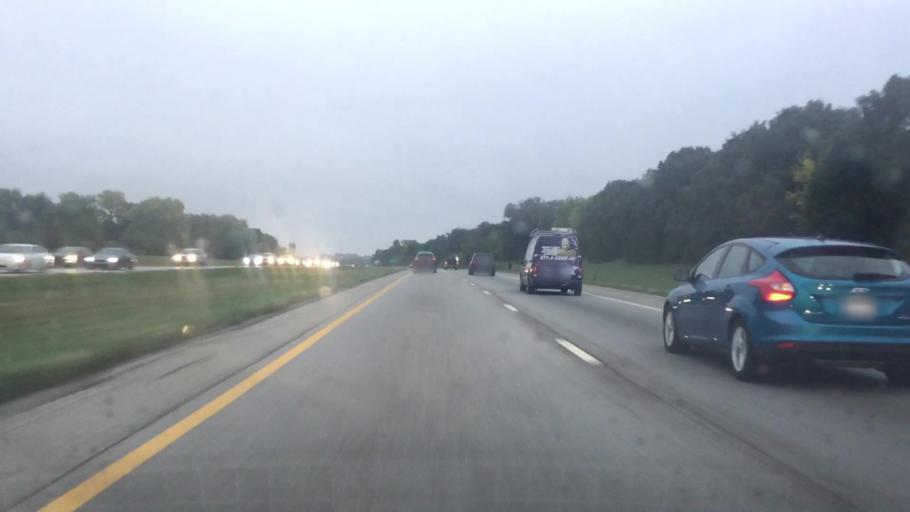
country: US
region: Kansas
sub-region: Johnson County
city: Lenexa
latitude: 38.8638
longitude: -94.6776
